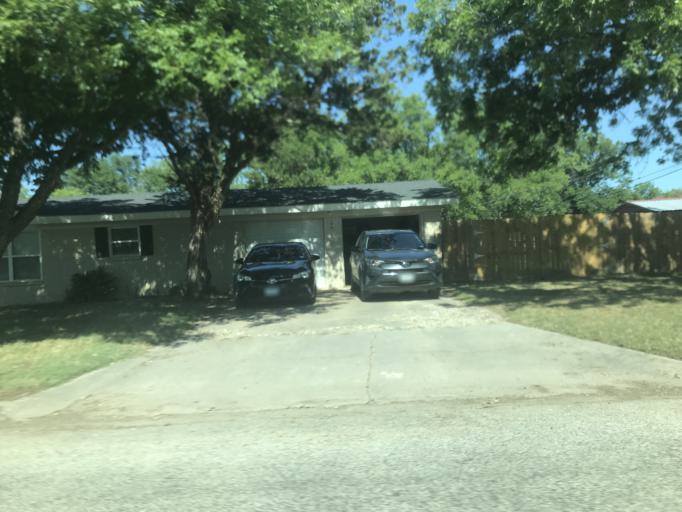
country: US
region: Texas
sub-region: Taylor County
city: Abilene
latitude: 32.4094
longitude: -99.7511
